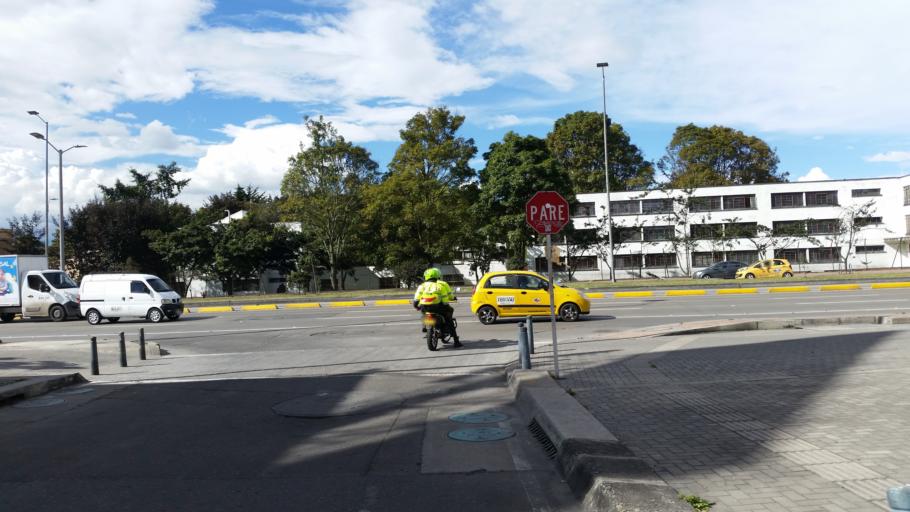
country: CO
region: Bogota D.C.
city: Bogota
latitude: 4.6336
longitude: -74.0856
